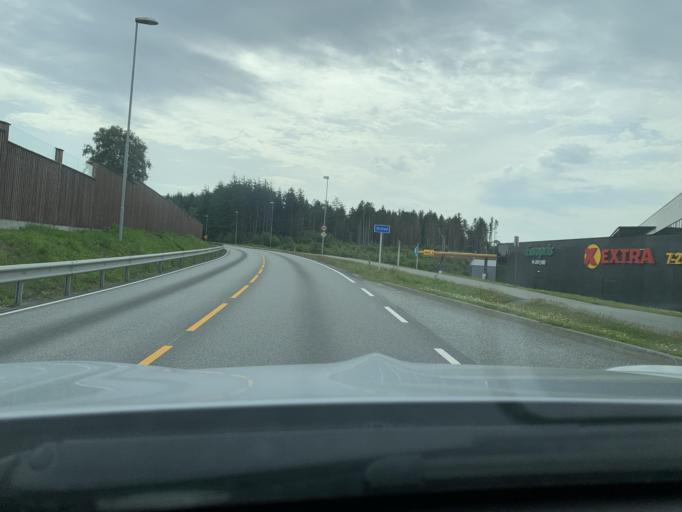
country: NO
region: Rogaland
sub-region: Sandnes
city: Sandnes
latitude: 58.7857
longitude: 5.7063
